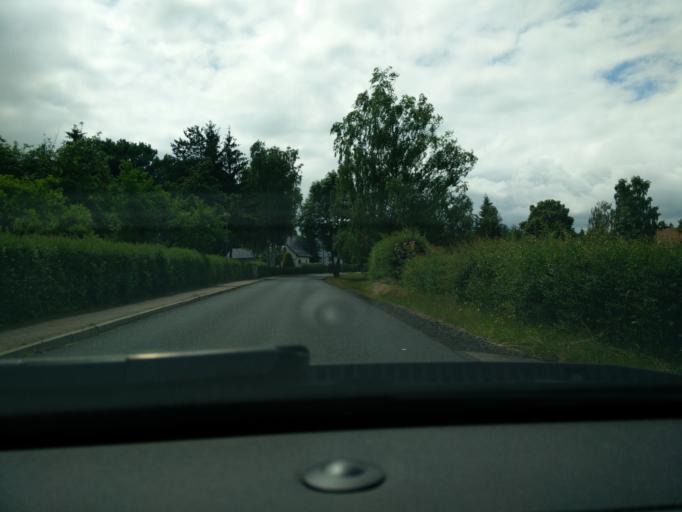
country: DE
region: Saxony
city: Bad Lausick
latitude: 51.1514
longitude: 12.6600
